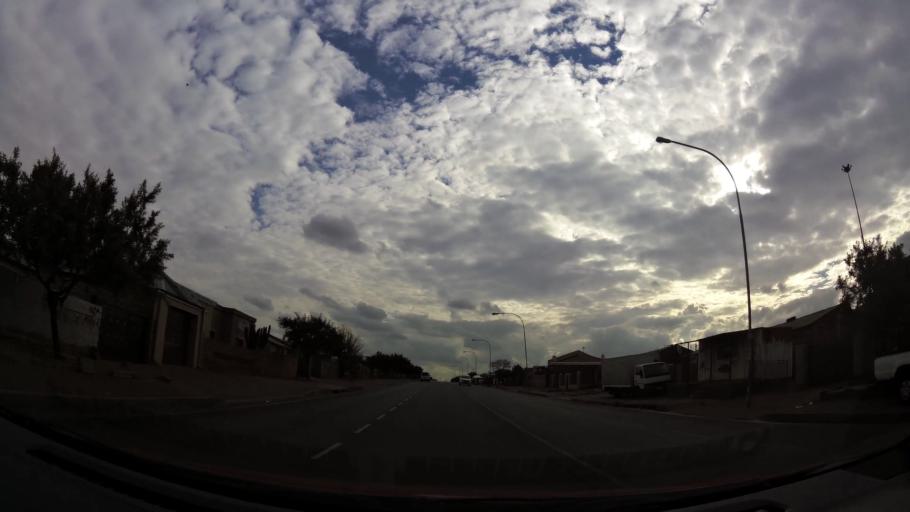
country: ZA
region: Gauteng
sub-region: City of Johannesburg Metropolitan Municipality
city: Soweto
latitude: -26.2487
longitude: 27.8357
